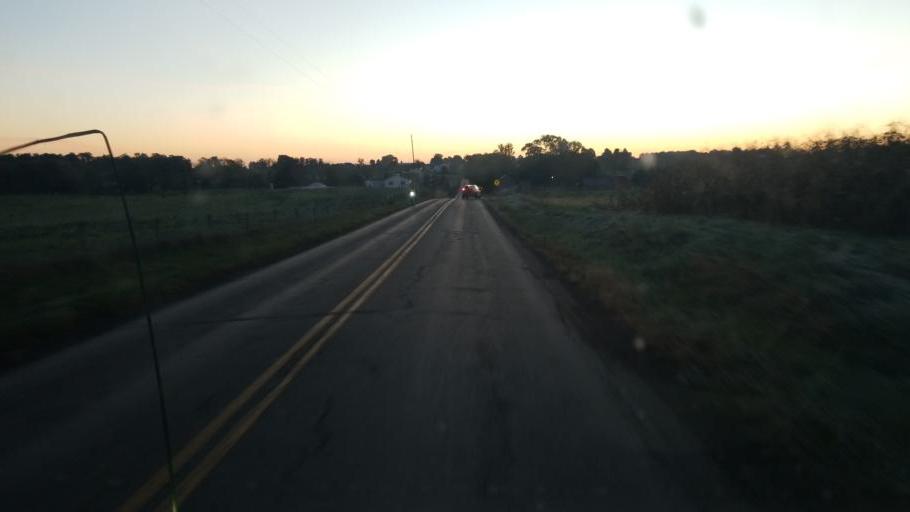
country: US
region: Ohio
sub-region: Wayne County
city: Apple Creek
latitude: 40.7411
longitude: -81.7890
